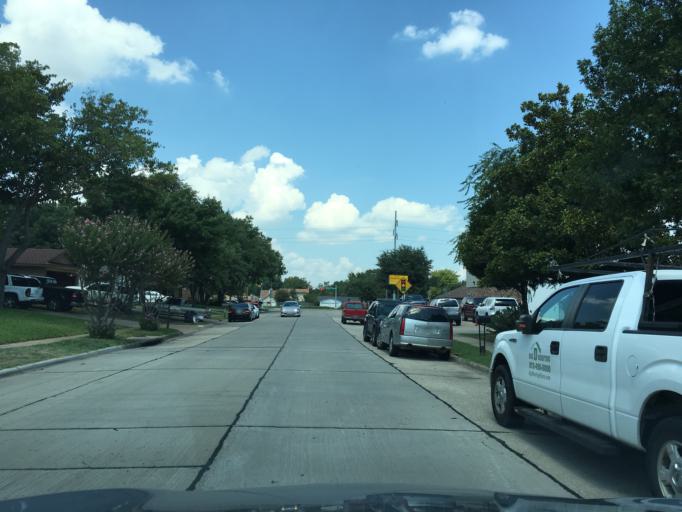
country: US
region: Texas
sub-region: Dallas County
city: Garland
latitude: 32.9438
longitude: -96.6569
